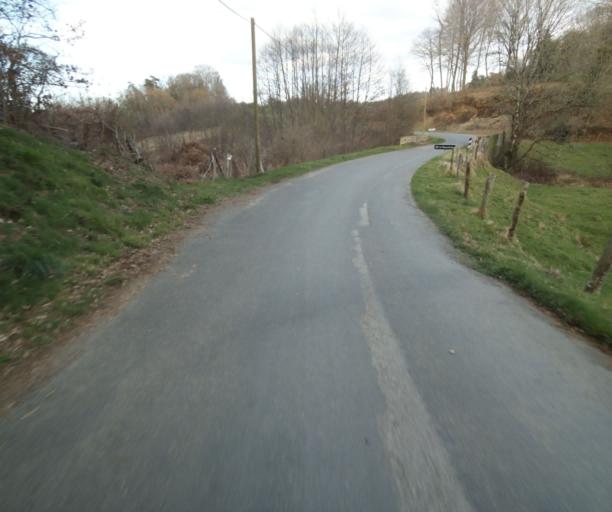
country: FR
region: Limousin
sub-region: Departement de la Correze
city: Saint-Clement
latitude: 45.3621
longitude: 1.6129
